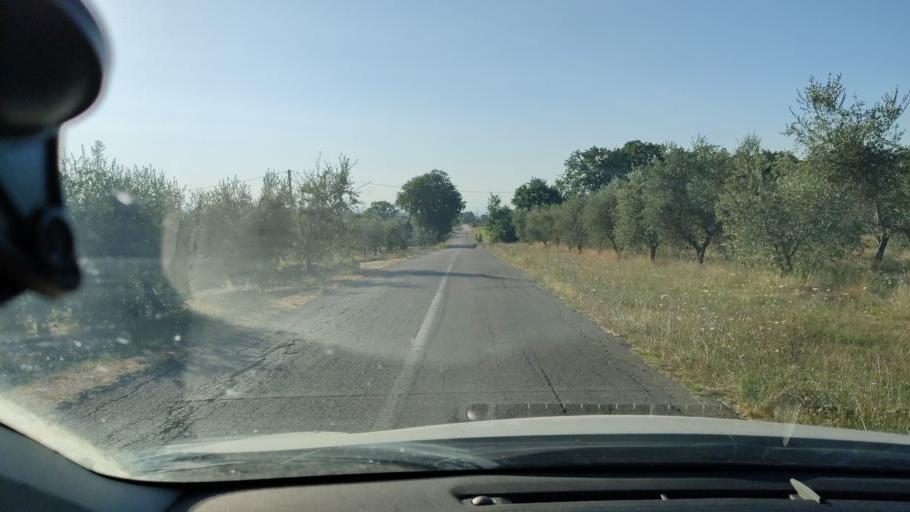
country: IT
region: Umbria
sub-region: Provincia di Terni
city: Lugnano in Teverina
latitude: 42.5459
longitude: 12.3519
